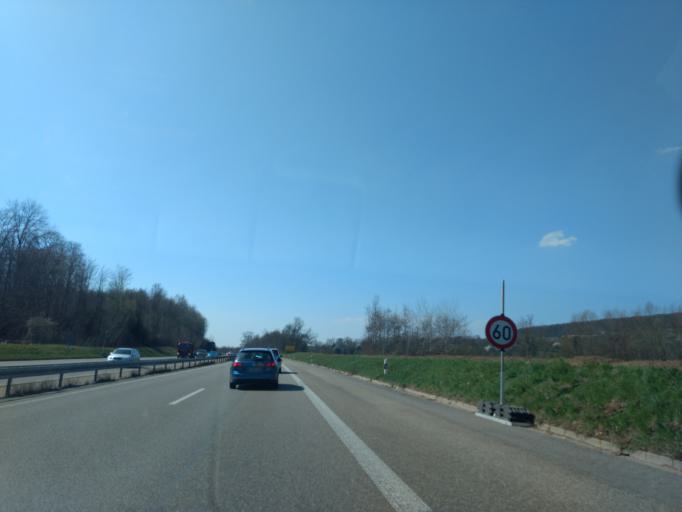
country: DE
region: Baden-Wuerttemberg
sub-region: Regierungsbezirk Stuttgart
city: Ebersbach an der Fils
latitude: 48.7112
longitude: 9.4962
